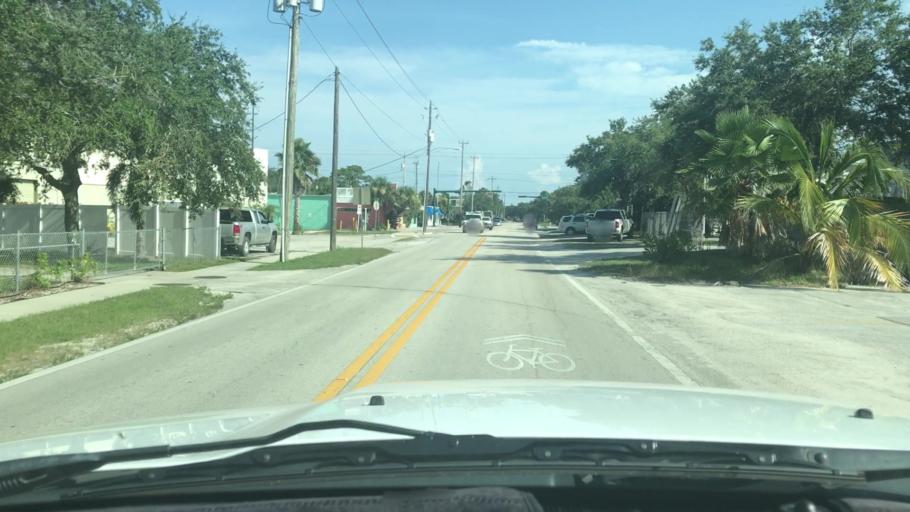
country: US
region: Florida
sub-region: Indian River County
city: Vero Beach
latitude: 27.6330
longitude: -80.3973
